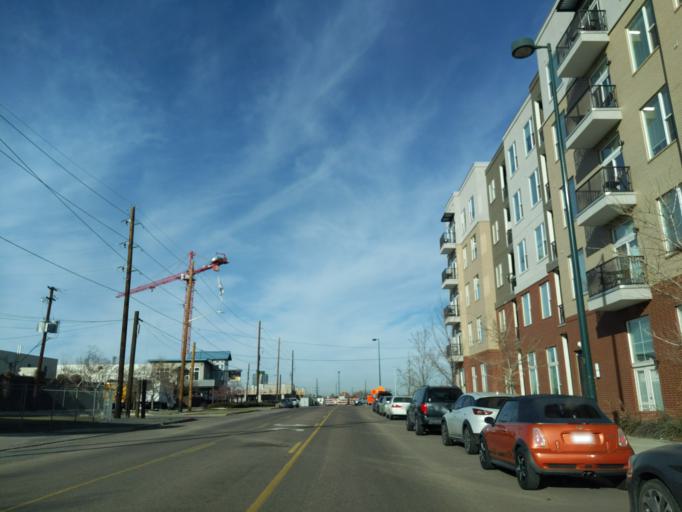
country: US
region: Colorado
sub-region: Denver County
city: Denver
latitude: 39.7620
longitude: -104.9910
